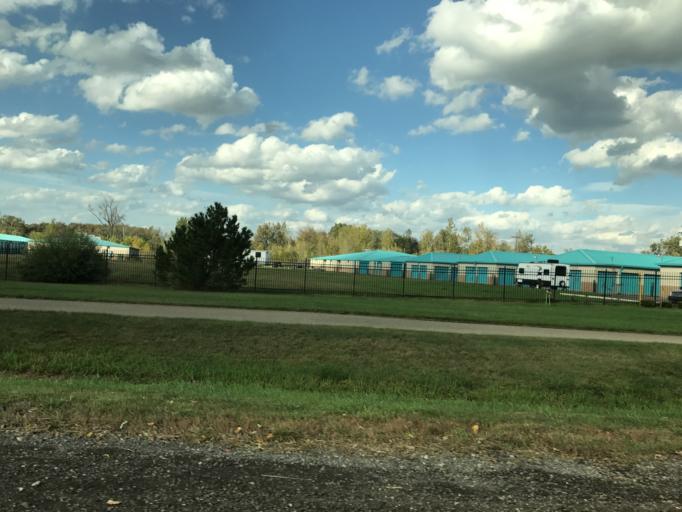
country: US
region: Michigan
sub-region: Oakland County
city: Wixom
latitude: 42.4999
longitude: -83.5613
